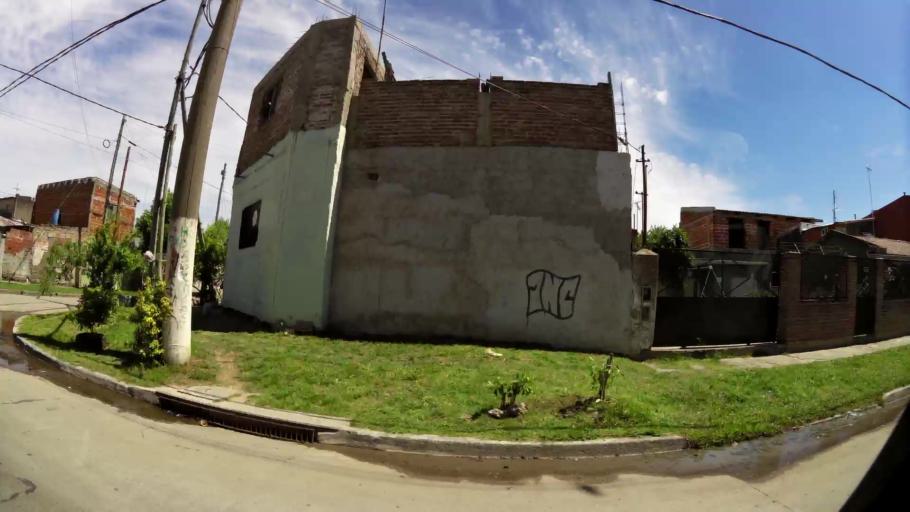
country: AR
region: Buenos Aires
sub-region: Partido de Quilmes
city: Quilmes
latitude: -34.7415
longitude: -58.3049
